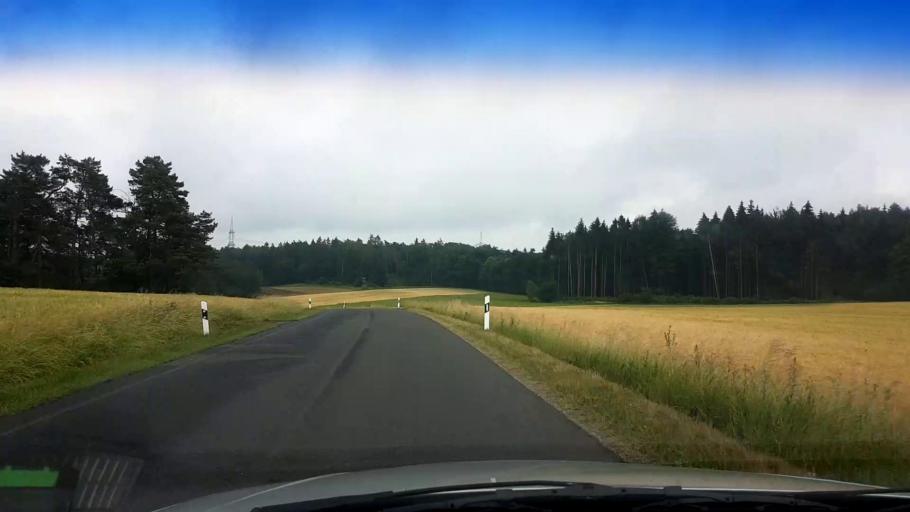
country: DE
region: Bavaria
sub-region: Upper Franconia
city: Wattendorf
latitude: 50.0517
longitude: 11.1258
